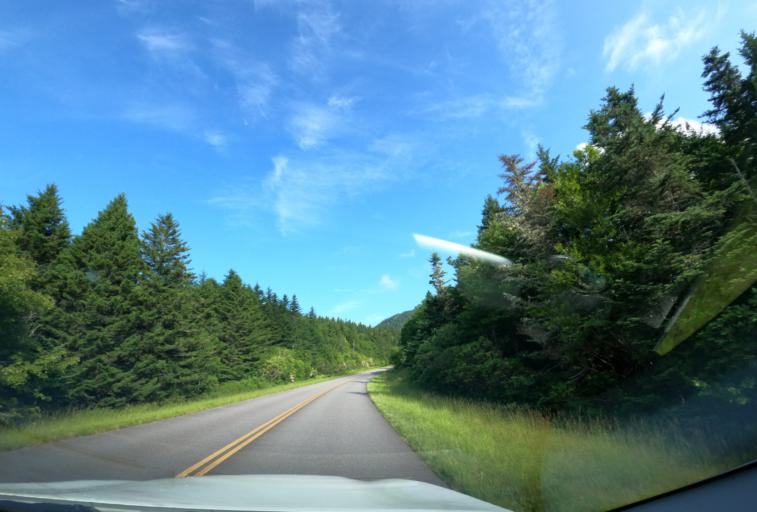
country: US
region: North Carolina
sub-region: Haywood County
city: Hazelwood
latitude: 35.2966
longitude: -82.9182
